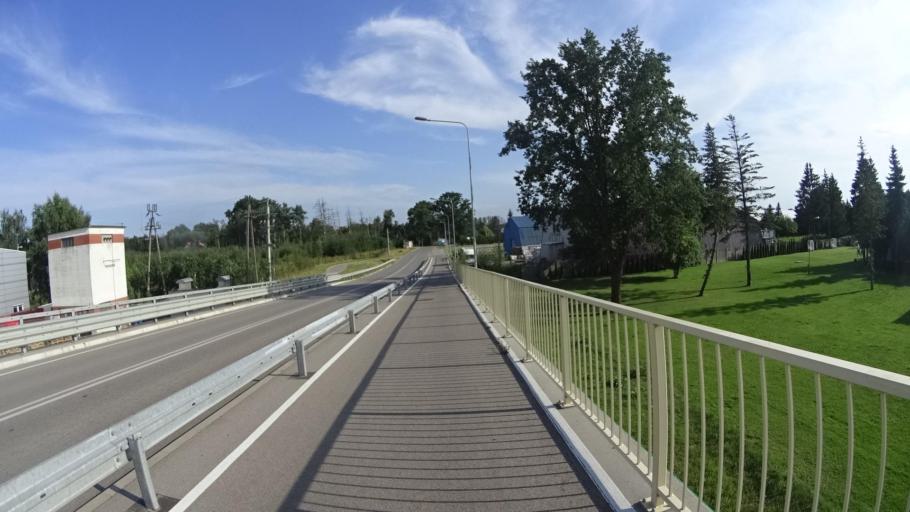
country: PL
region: Masovian Voivodeship
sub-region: Powiat pruszkowski
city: Nadarzyn
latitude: 52.0824
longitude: 20.7944
